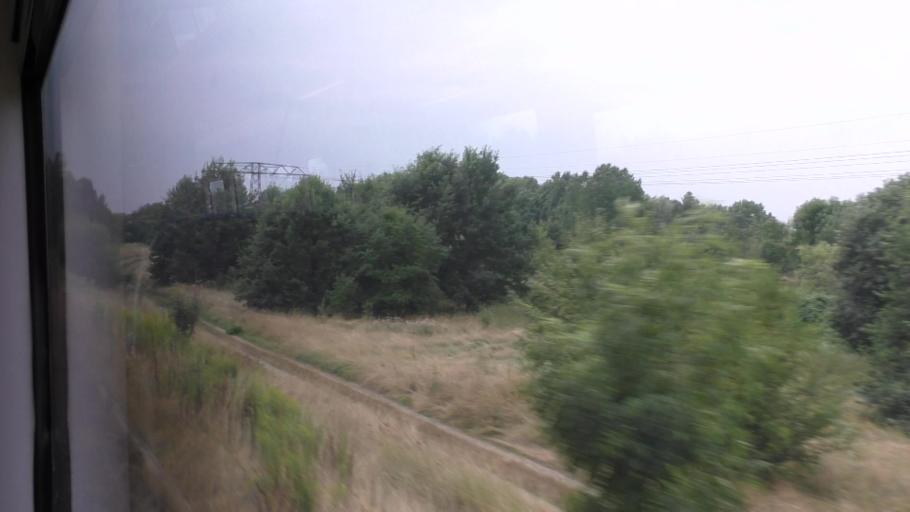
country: DE
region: Saxony
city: Goerlitz
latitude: 51.1020
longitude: 14.9791
